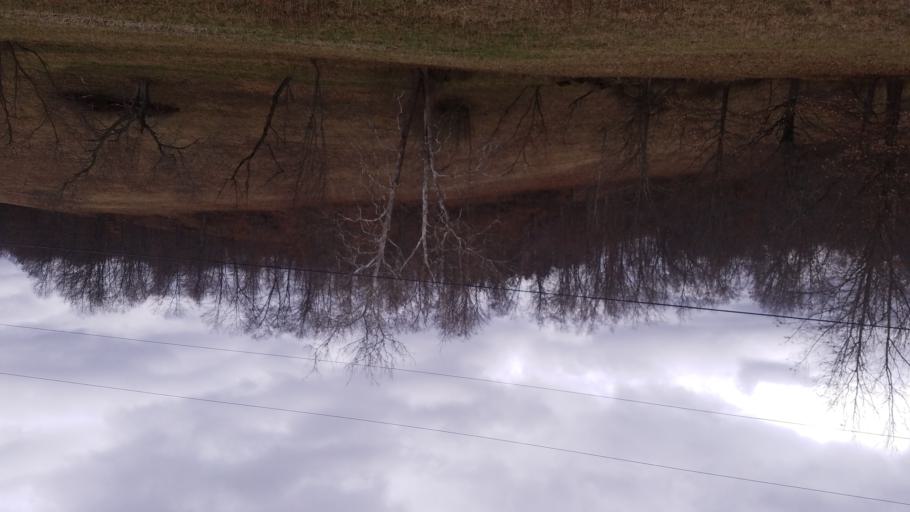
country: US
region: Ohio
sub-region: Licking County
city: Newark
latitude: 40.1741
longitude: -82.3191
